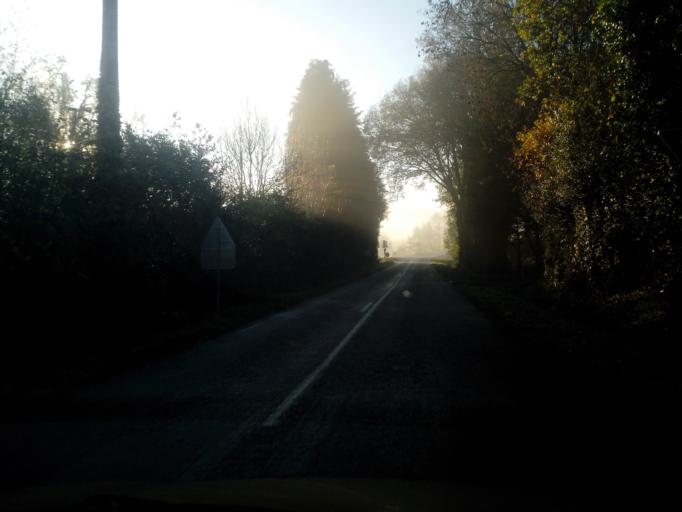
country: FR
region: Brittany
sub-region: Departement du Morbihan
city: Pluherlin
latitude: 47.7125
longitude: -2.3375
